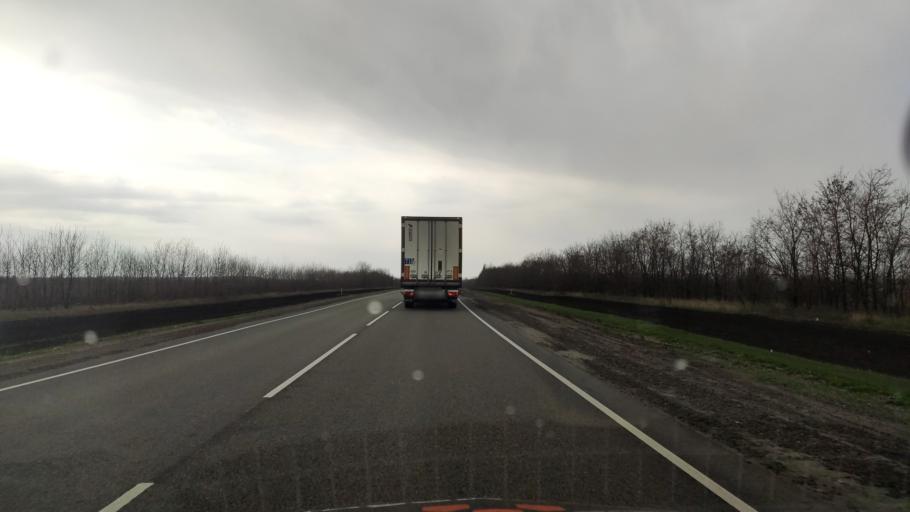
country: RU
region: Voronezj
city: Nizhnedevitsk
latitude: 51.5685
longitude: 38.3388
